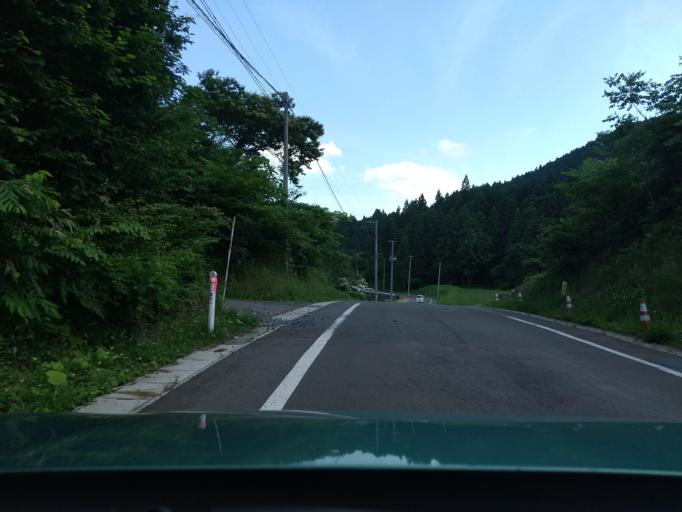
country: JP
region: Iwate
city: Ichinoseki
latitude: 38.9984
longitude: 141.2185
